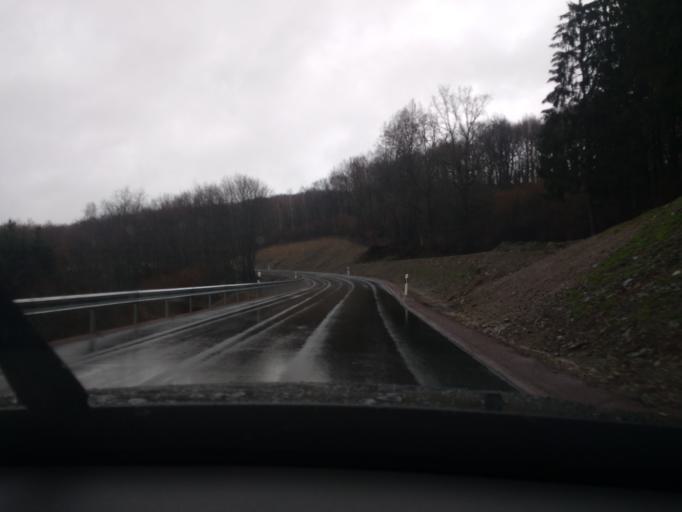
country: DE
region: Rheinland-Pfalz
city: Hinzenburg
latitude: 49.6577
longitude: 6.7346
